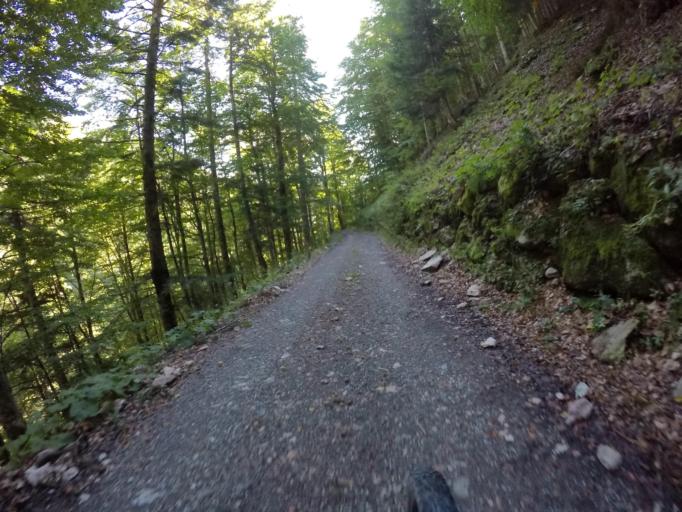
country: IT
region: Friuli Venezia Giulia
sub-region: Provincia di Udine
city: Ligosullo
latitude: 46.5806
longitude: 13.0994
